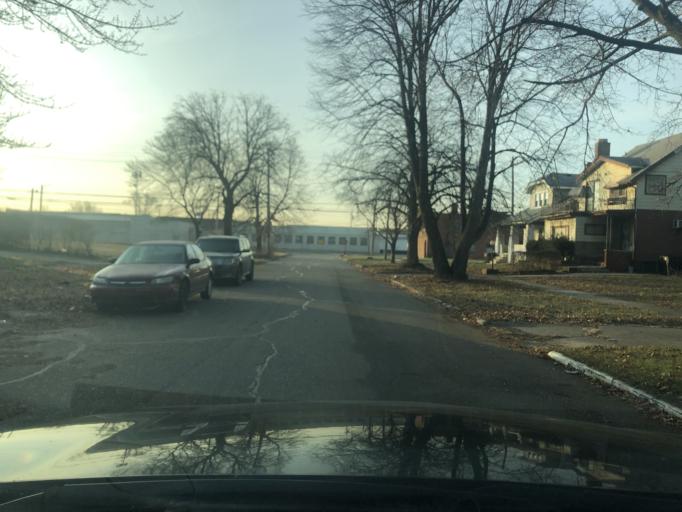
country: US
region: Michigan
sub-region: Wayne County
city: Highland Park
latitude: 42.4041
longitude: -83.1261
